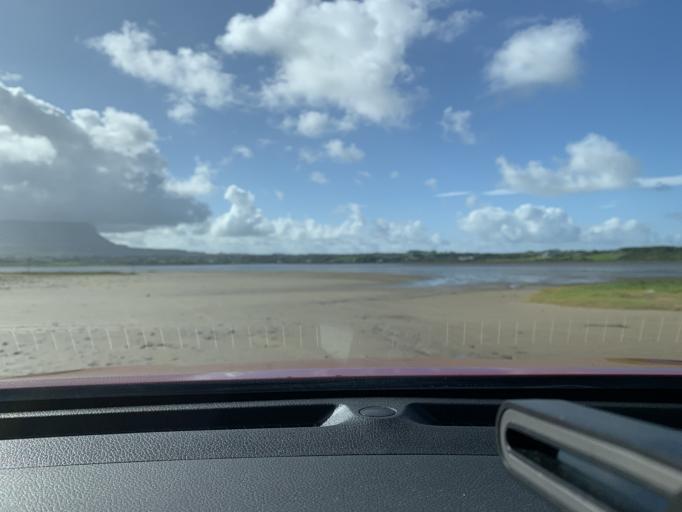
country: IE
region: Connaught
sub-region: Sligo
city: Strandhill
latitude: 54.4043
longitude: -8.5599
